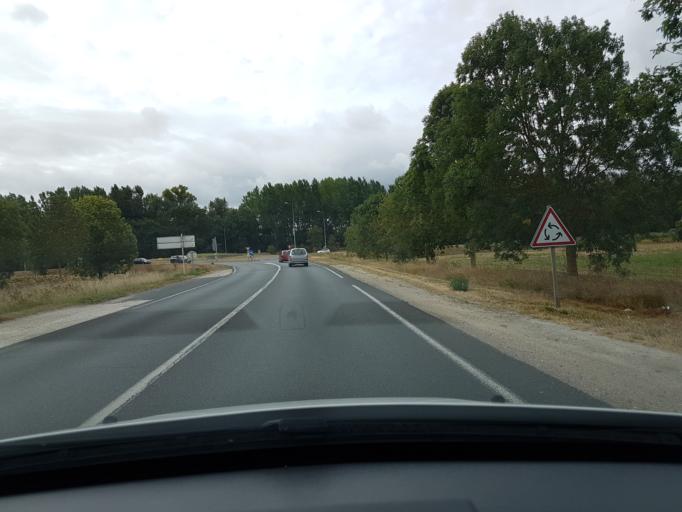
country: FR
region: Centre
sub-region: Departement d'Indre-et-Loire
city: Larcay
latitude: 47.3827
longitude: 0.7840
